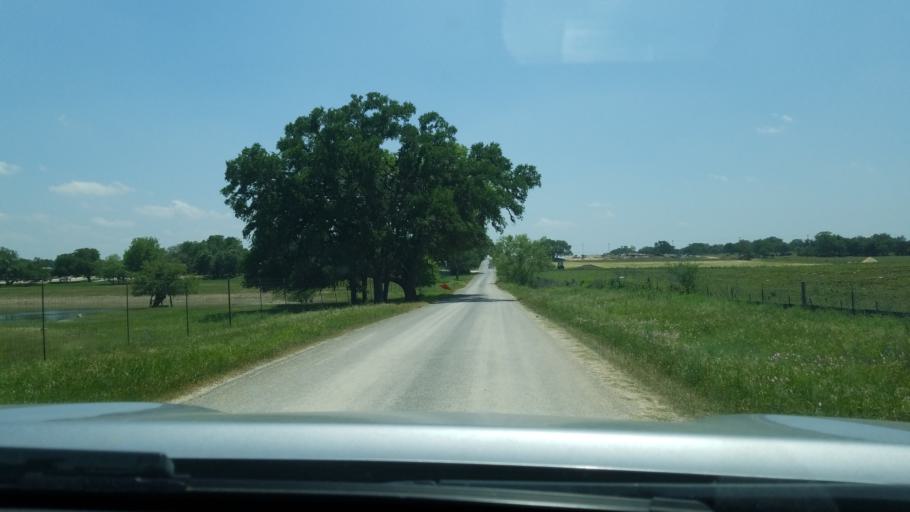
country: US
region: Texas
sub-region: Blanco County
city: Blanco
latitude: 30.0736
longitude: -98.3971
